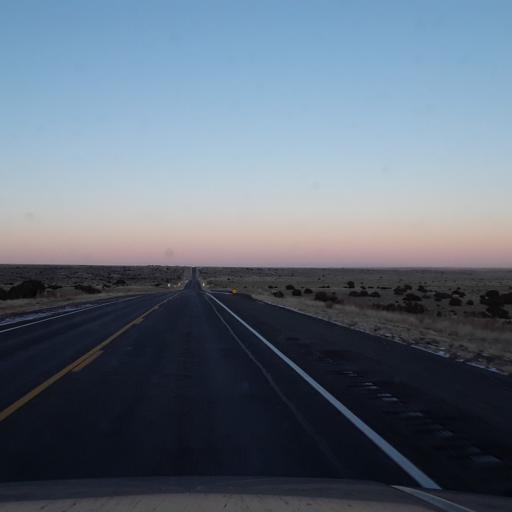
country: US
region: New Mexico
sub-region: Guadalupe County
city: Santa Rosa
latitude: 34.5340
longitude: -105.3168
